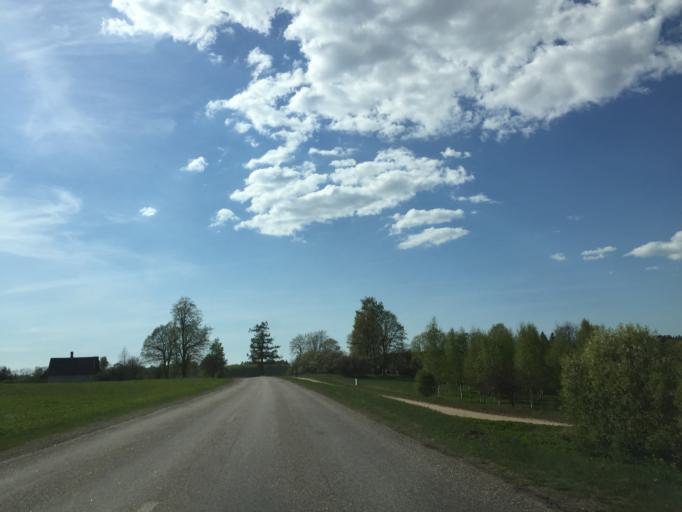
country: LV
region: Limbazu Rajons
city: Limbazi
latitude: 57.5130
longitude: 24.7902
